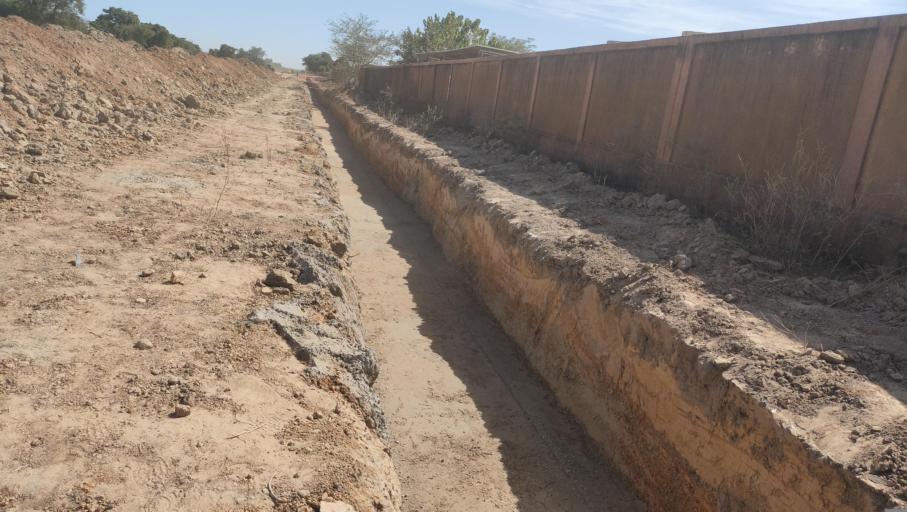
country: BF
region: Est
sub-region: Province du Gourma
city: Fada N'gourma
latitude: 12.0731
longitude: 0.3274
